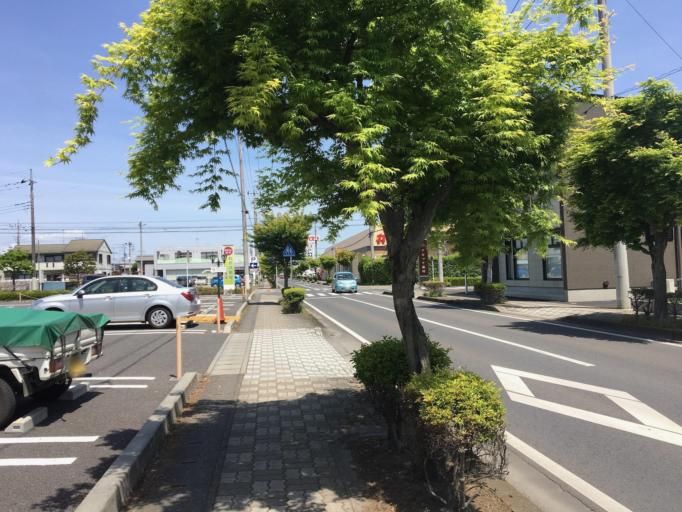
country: JP
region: Tochigi
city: Mibu
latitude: 36.4320
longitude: 139.8024
